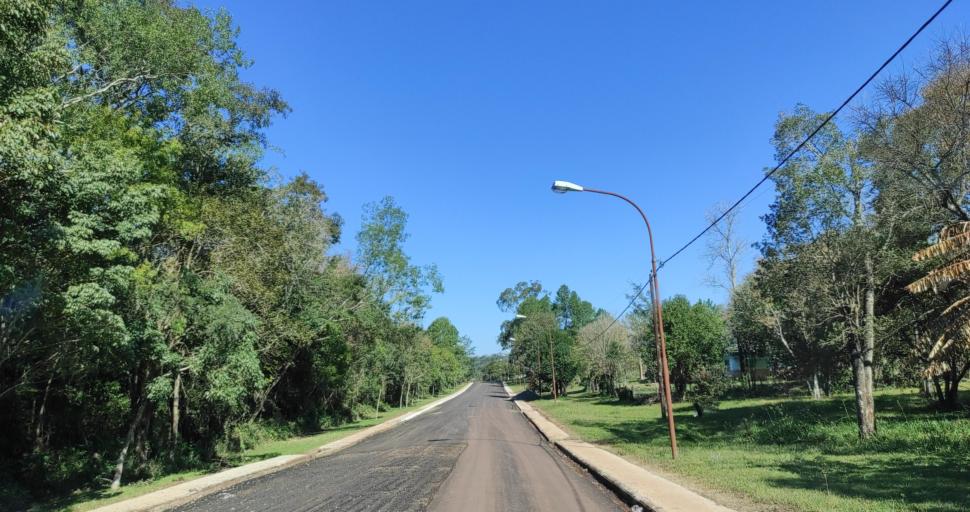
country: AR
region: Misiones
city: Cerro Cora
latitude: -27.6310
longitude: -55.7038
